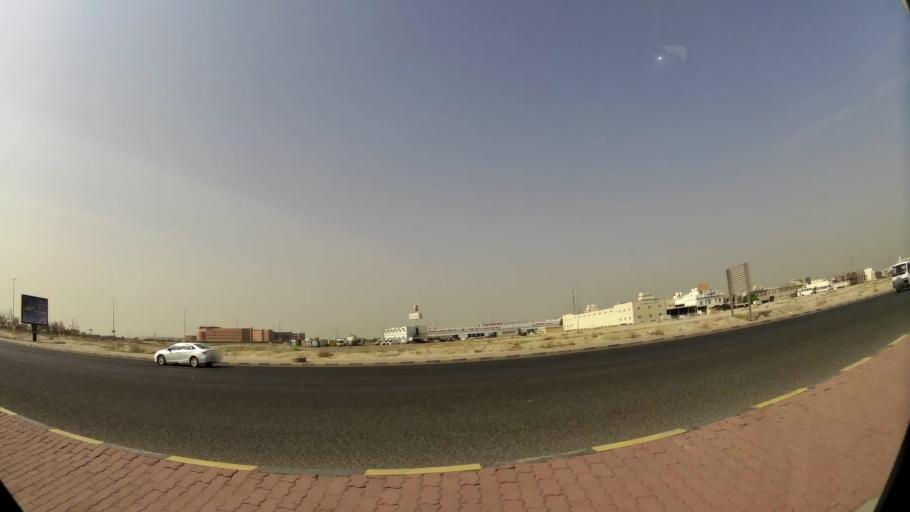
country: KW
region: Al Asimah
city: Ar Rabiyah
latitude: 29.2898
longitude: 47.9283
